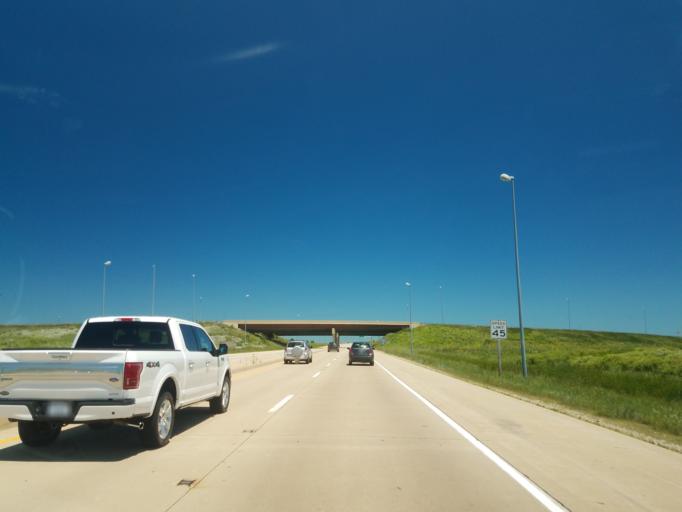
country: US
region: Illinois
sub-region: McLean County
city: Normal
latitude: 40.5362
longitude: -88.9502
